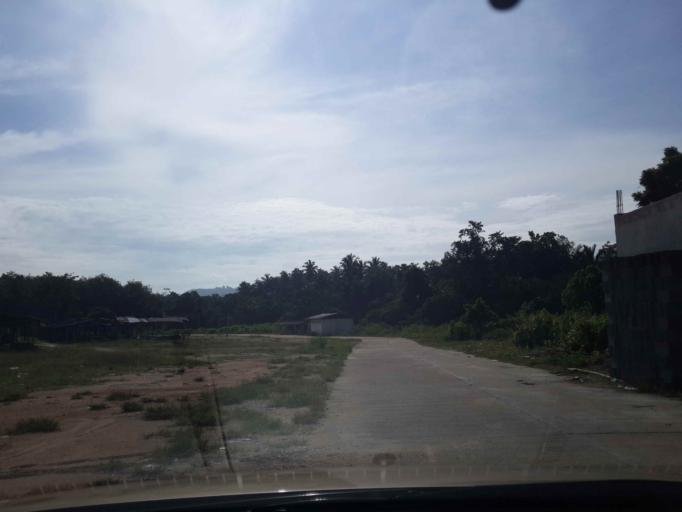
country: TH
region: Narathiwat
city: Rueso
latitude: 6.3823
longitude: 101.5116
